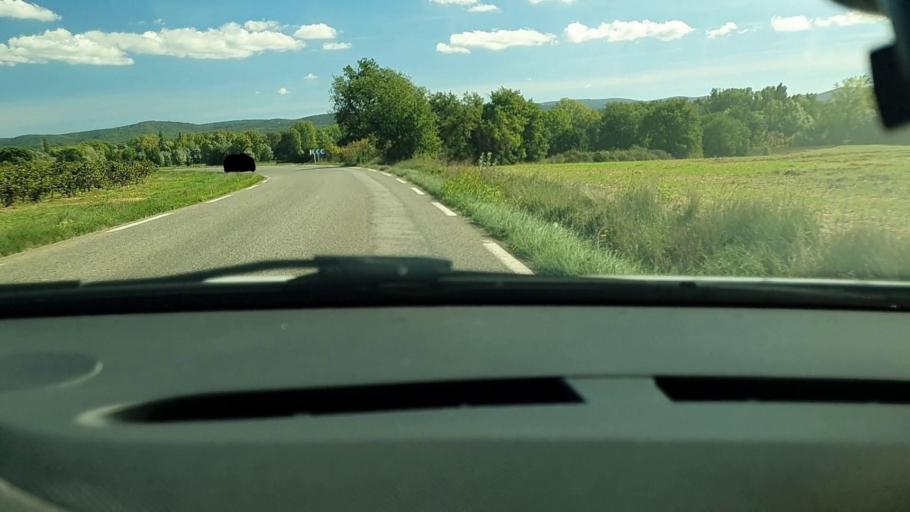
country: FR
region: Languedoc-Roussillon
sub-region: Departement du Gard
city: Saint-Ambroix
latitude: 44.2342
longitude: 4.2562
